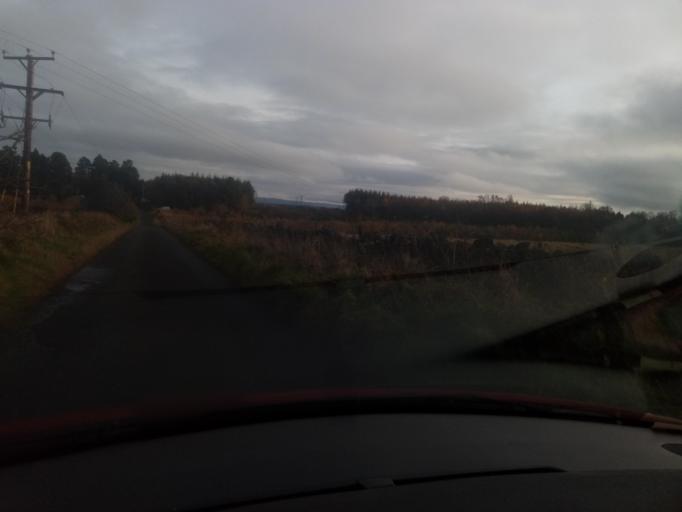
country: GB
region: Scotland
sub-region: The Scottish Borders
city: Jedburgh
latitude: 55.4824
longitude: -2.5786
